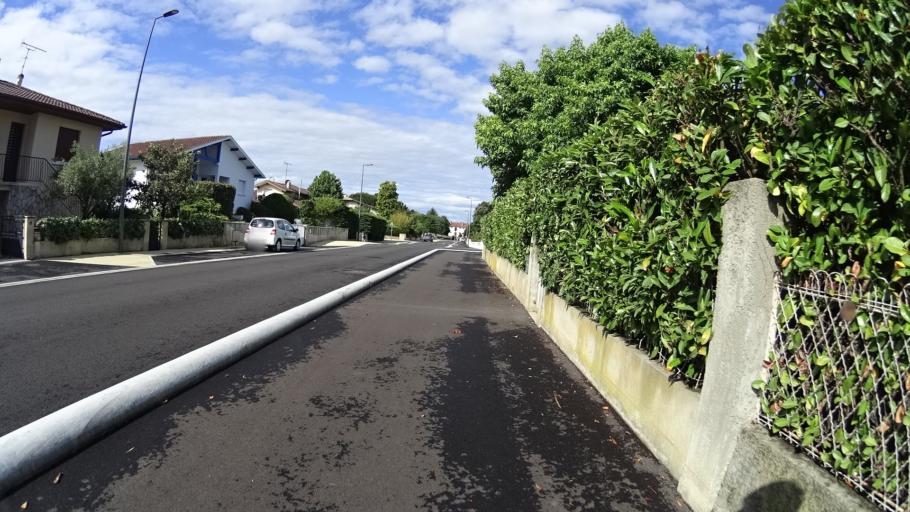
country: FR
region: Aquitaine
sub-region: Departement des Landes
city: Dax
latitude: 43.6990
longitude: -1.0709
